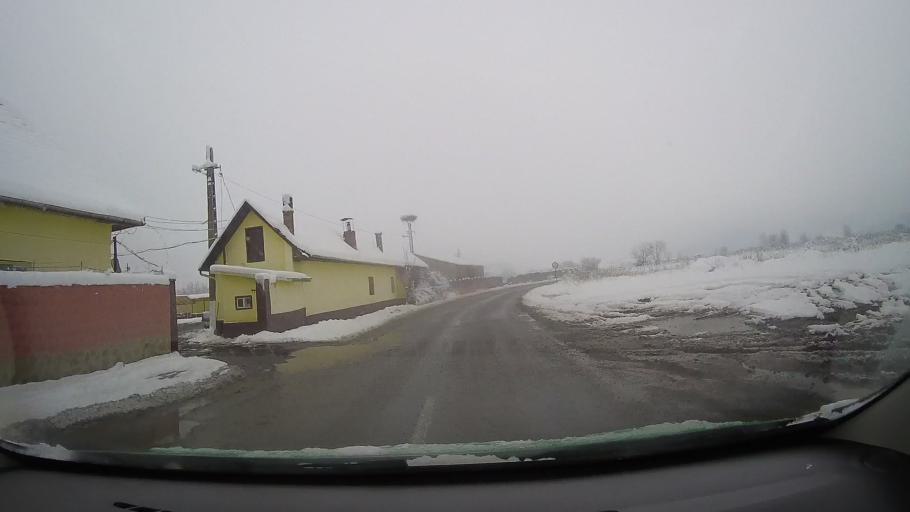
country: RO
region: Sibiu
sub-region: Comuna Orlat
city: Orlat
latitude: 45.7819
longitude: 23.9444
